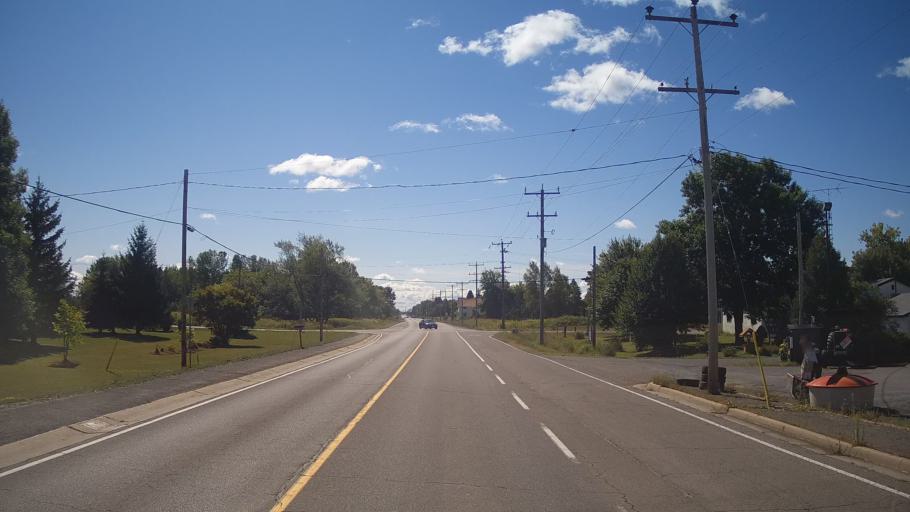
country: US
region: New York
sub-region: St. Lawrence County
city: Norfolk
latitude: 44.9358
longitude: -75.2129
